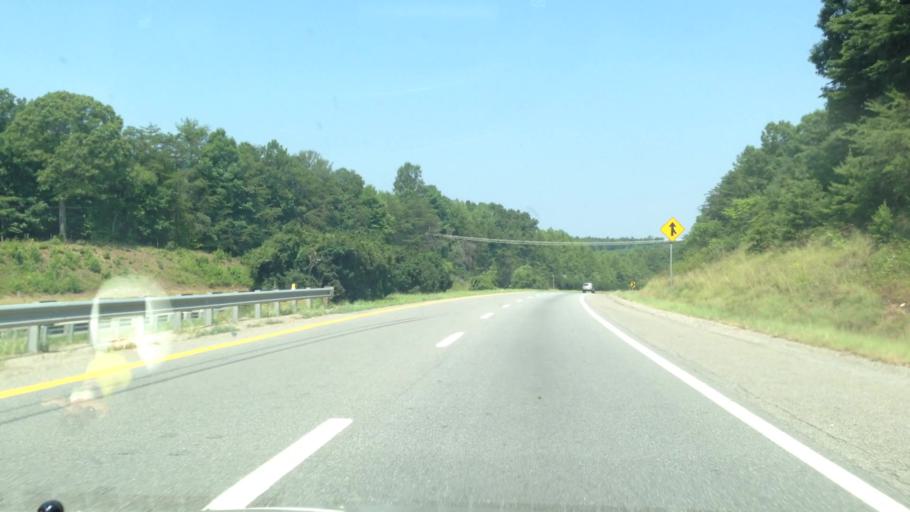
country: US
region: Virginia
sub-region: Henry County
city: Horse Pasture
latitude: 36.6490
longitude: -79.9161
